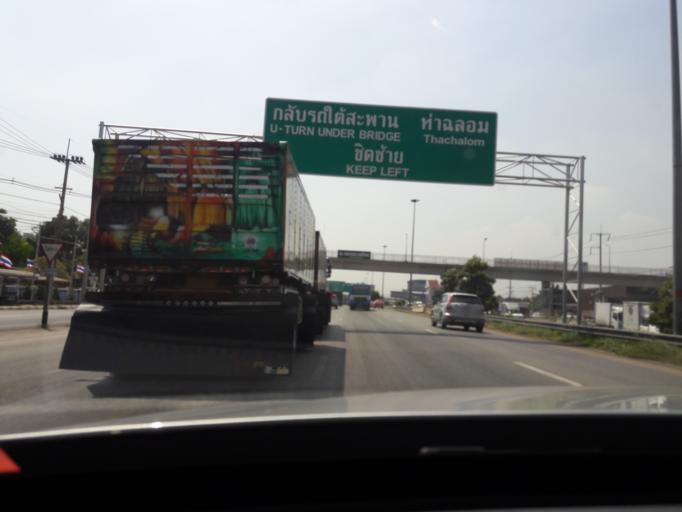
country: TH
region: Samut Sakhon
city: Samut Sakhon
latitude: 13.5504
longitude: 100.2638
